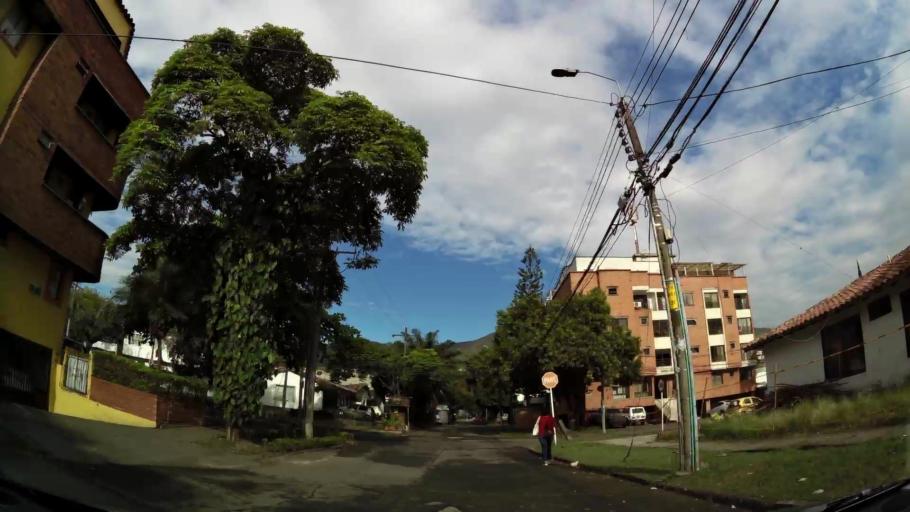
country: CO
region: Valle del Cauca
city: Cali
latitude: 3.4863
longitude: -76.5224
